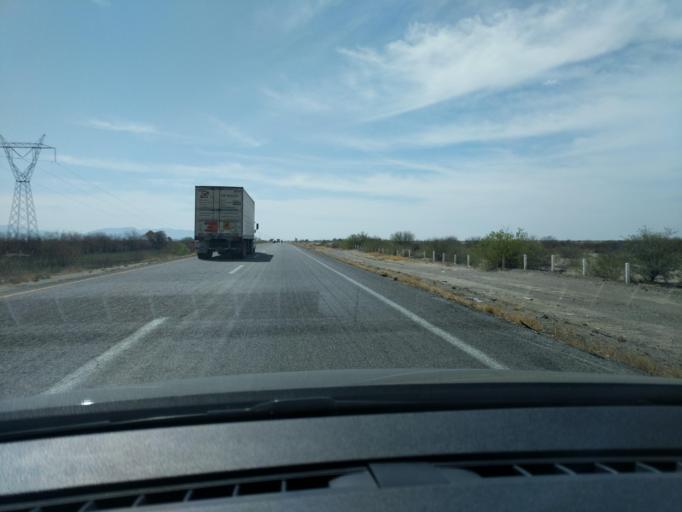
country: MX
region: Coahuila
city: Viesca
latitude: 25.6654
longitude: -102.5807
